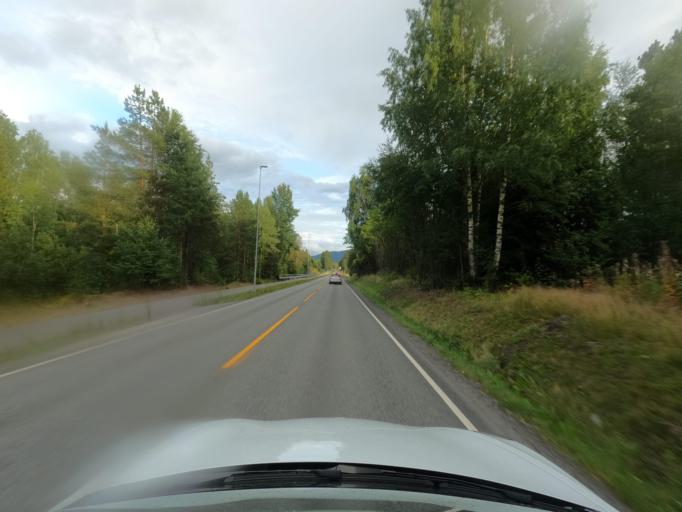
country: NO
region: Telemark
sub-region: Notodden
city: Notodden
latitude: 59.5879
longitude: 9.1572
